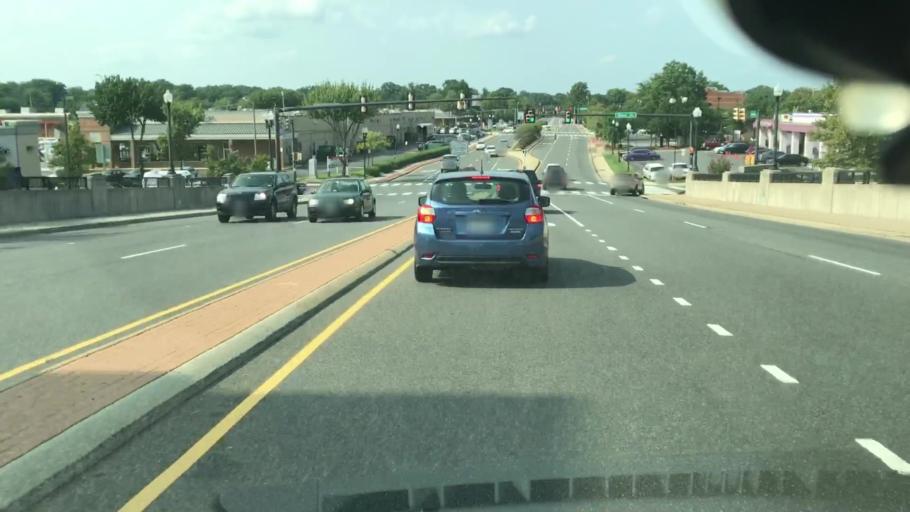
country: US
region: Virginia
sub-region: Fairfax County
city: Springfield
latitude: 38.7801
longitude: -77.1860
